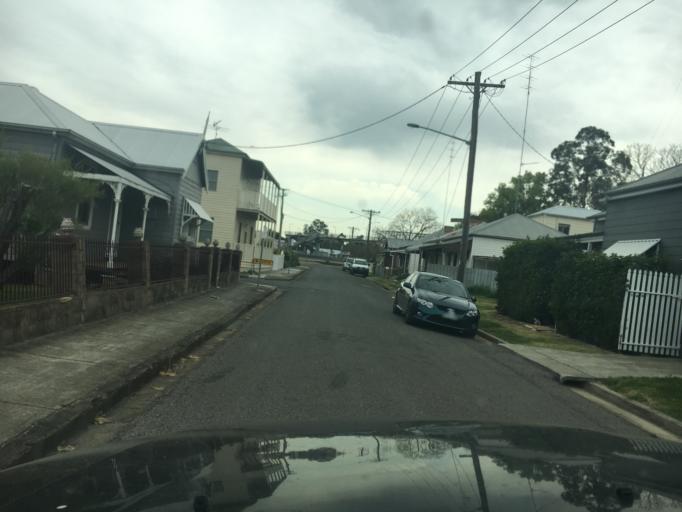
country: AU
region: New South Wales
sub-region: Maitland Municipality
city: Lorn
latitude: -32.7428
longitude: 151.5629
